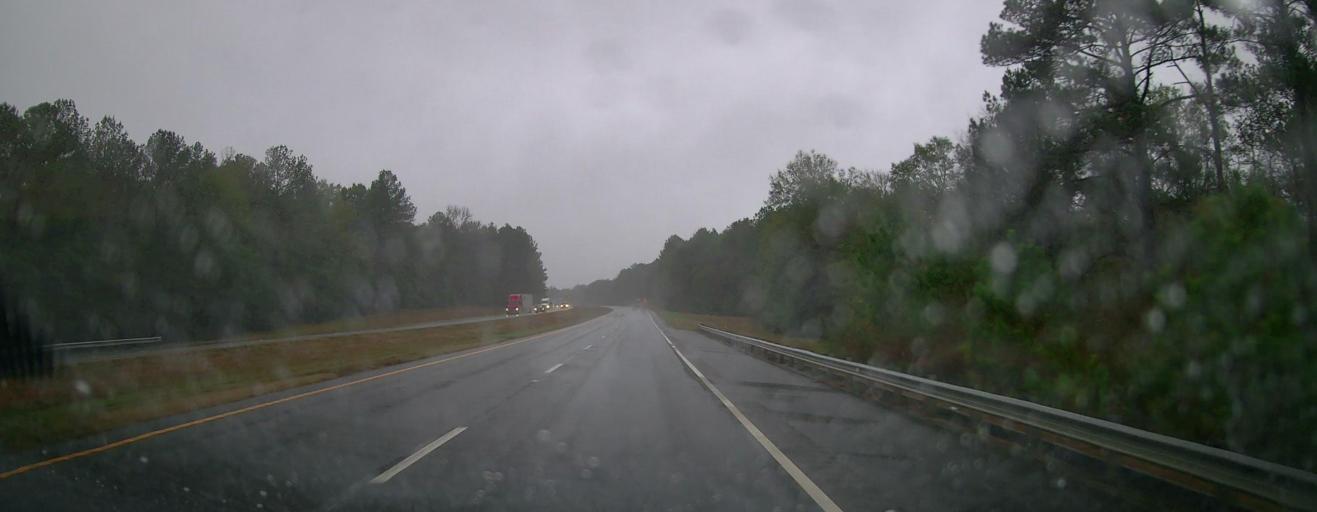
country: US
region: Georgia
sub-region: Putnam County
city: Eatonton
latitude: 33.3034
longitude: -83.3921
